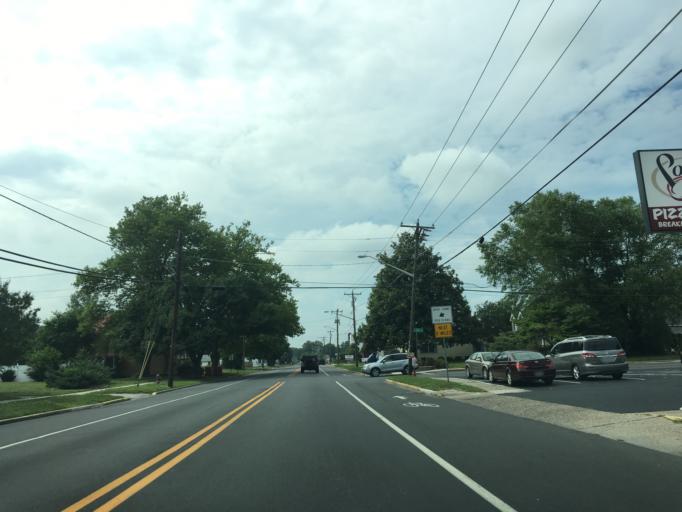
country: US
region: Delaware
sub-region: Sussex County
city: Millsboro
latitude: 38.5496
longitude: -75.2458
